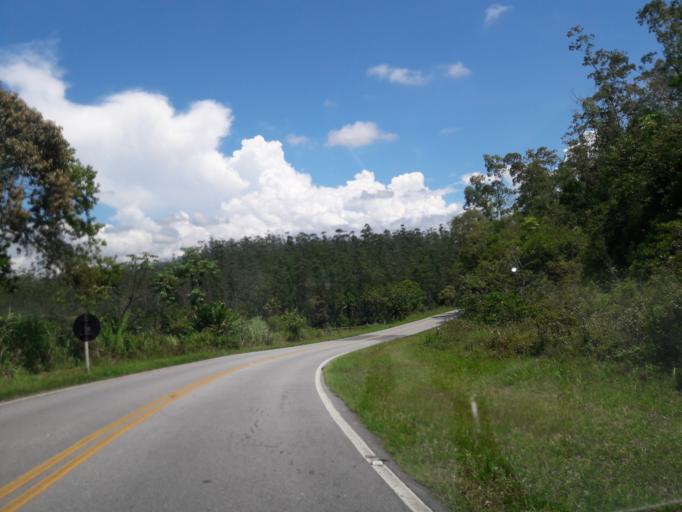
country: BR
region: Parana
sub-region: Antonina
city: Antonina
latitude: -25.5258
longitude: -48.7741
